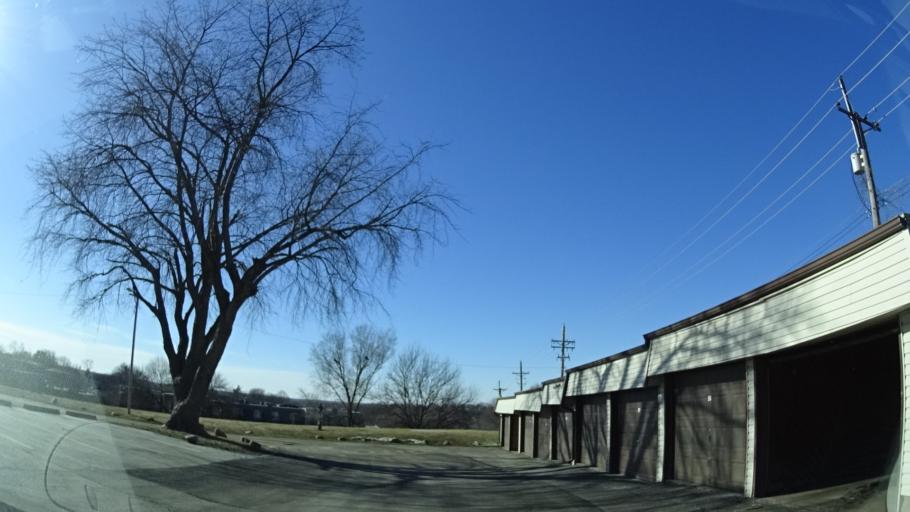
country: US
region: Nebraska
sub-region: Sarpy County
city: Bellevue
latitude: 41.1471
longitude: -95.9109
